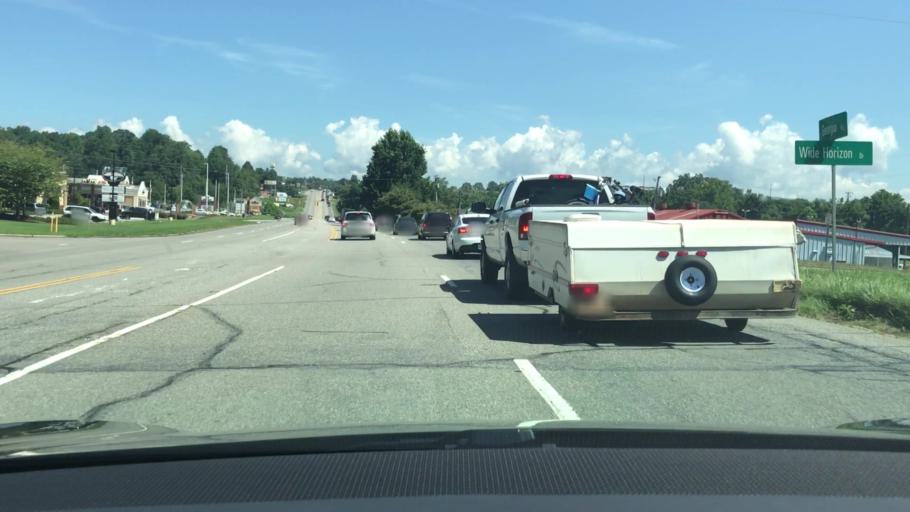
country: US
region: North Carolina
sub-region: Macon County
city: Franklin
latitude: 35.1542
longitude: -83.3917
